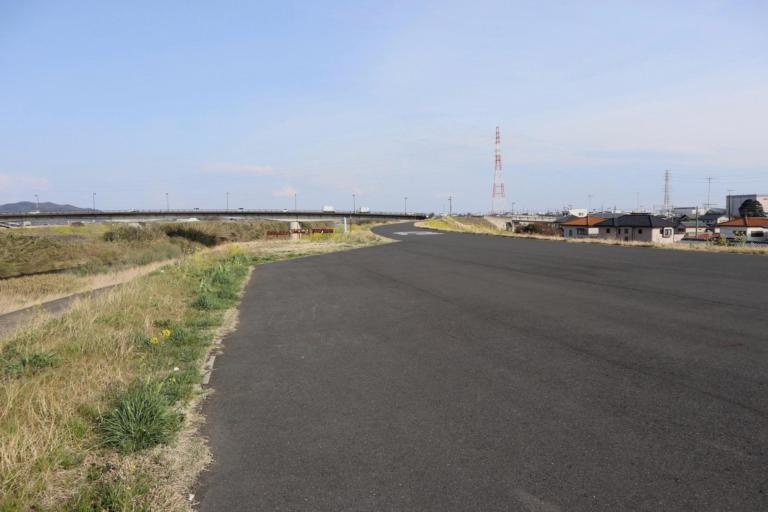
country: JP
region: Tochigi
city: Ashikaga
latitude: 36.3196
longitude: 139.4622
